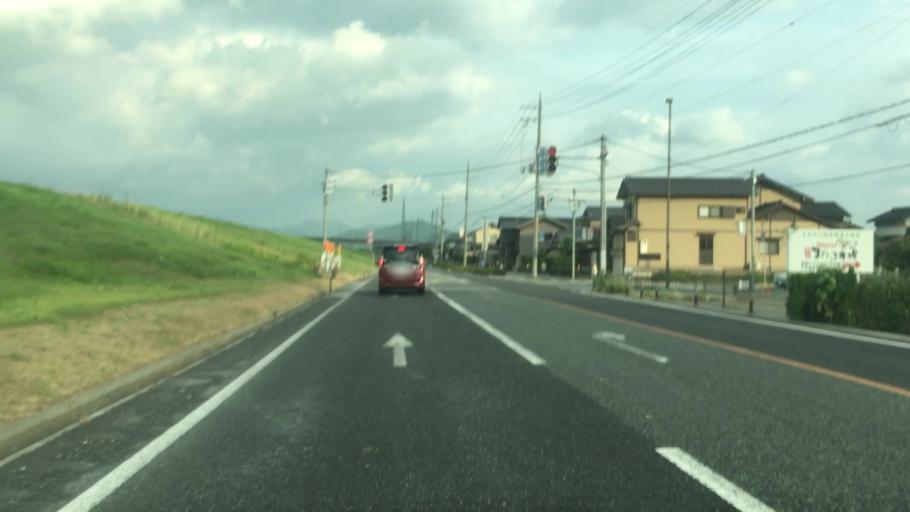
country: JP
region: Hyogo
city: Toyooka
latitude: 35.5588
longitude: 134.8159
